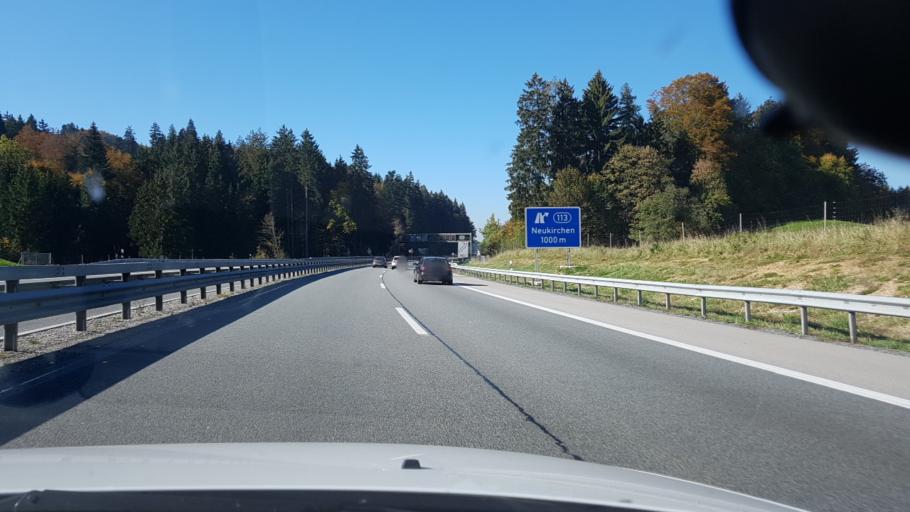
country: DE
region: Bavaria
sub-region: Upper Bavaria
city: Inzell
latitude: 47.8269
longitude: 12.7526
